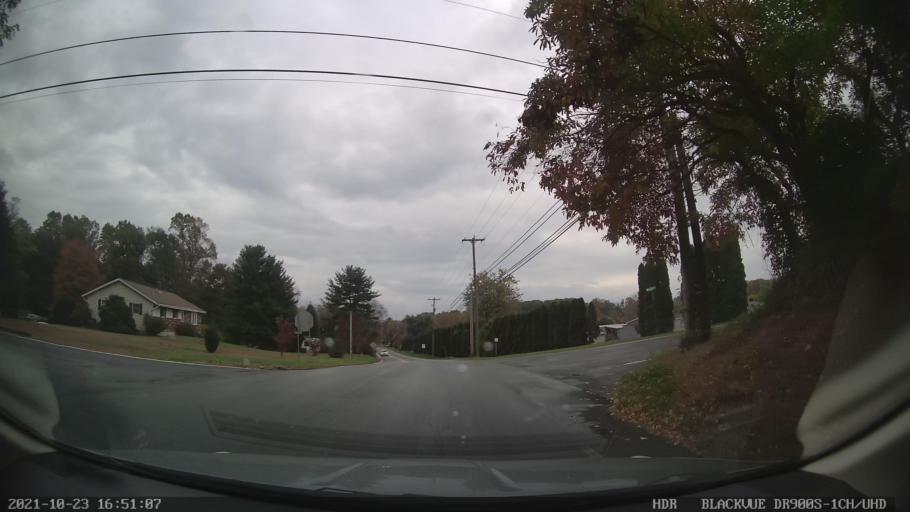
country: US
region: Pennsylvania
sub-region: Berks County
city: Red Lion
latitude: 40.4735
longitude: -75.6095
